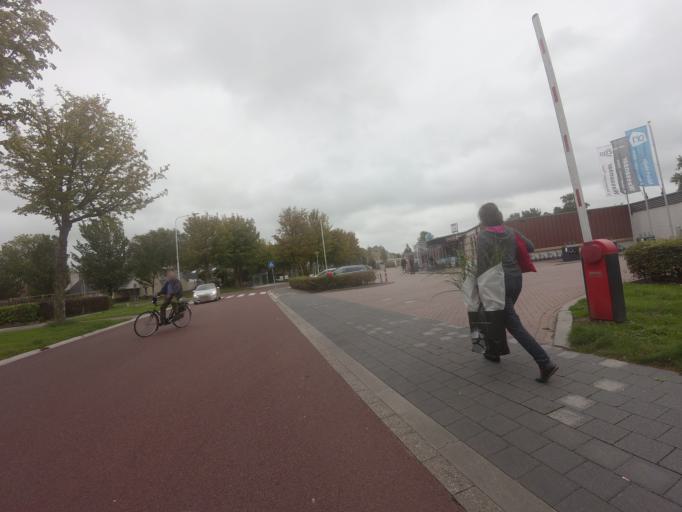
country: NL
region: Friesland
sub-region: Gemeente Leeuwarderadeel
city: Stiens
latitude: 53.2571
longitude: 5.7647
